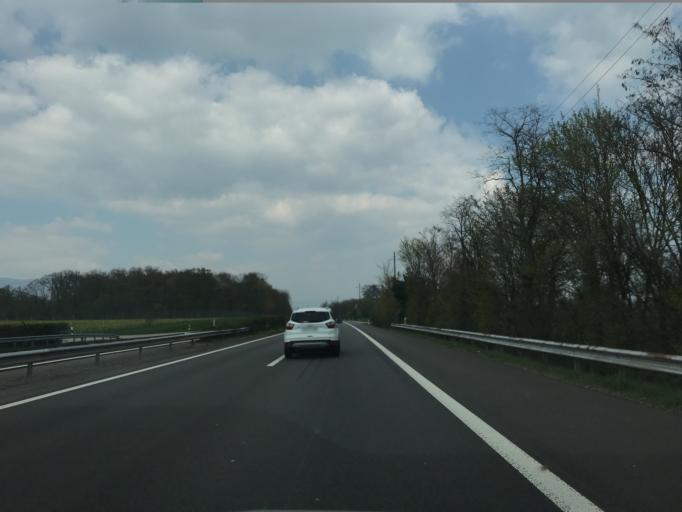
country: CH
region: Geneva
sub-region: Geneva
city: Versoix
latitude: 46.2836
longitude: 6.1447
